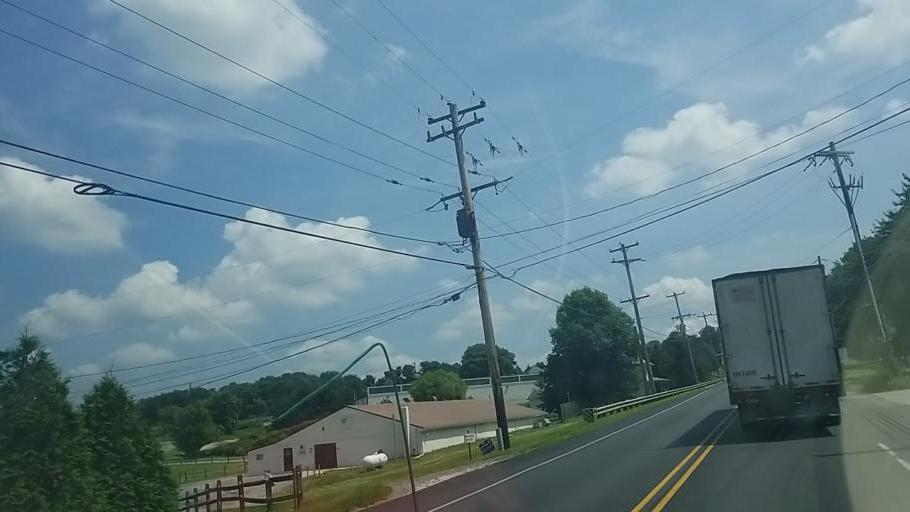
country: US
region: Pennsylvania
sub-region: Chester County
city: Avondale
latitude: 39.8175
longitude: -75.7703
